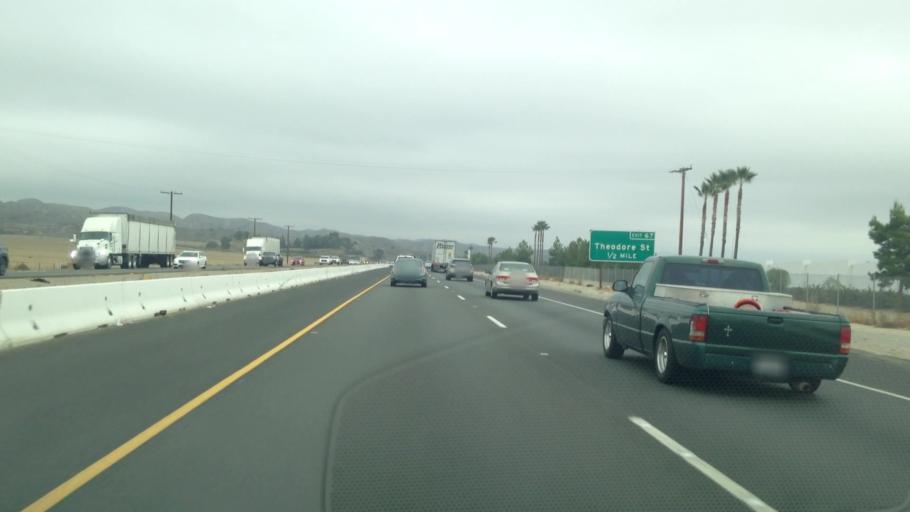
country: US
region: California
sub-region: Riverside County
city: Moreno Valley
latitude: 33.9392
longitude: -117.1511
